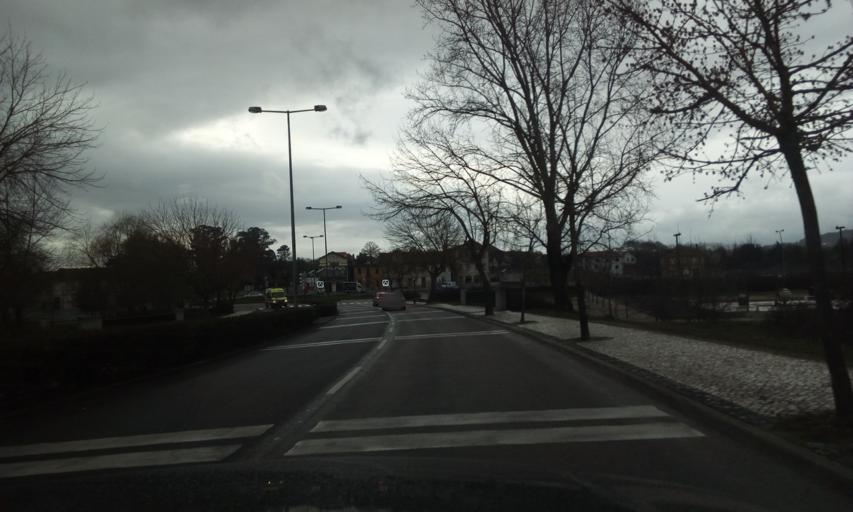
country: PT
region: Viseu
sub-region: Viseu
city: Viseu
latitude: 40.6642
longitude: -7.9063
